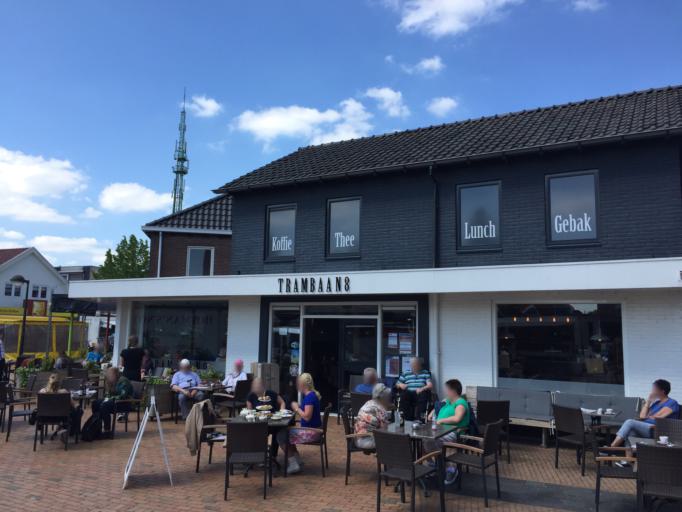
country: NL
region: Friesland
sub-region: Gemeente Heerenveen
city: Jubbega
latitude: 52.9891
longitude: 6.2913
